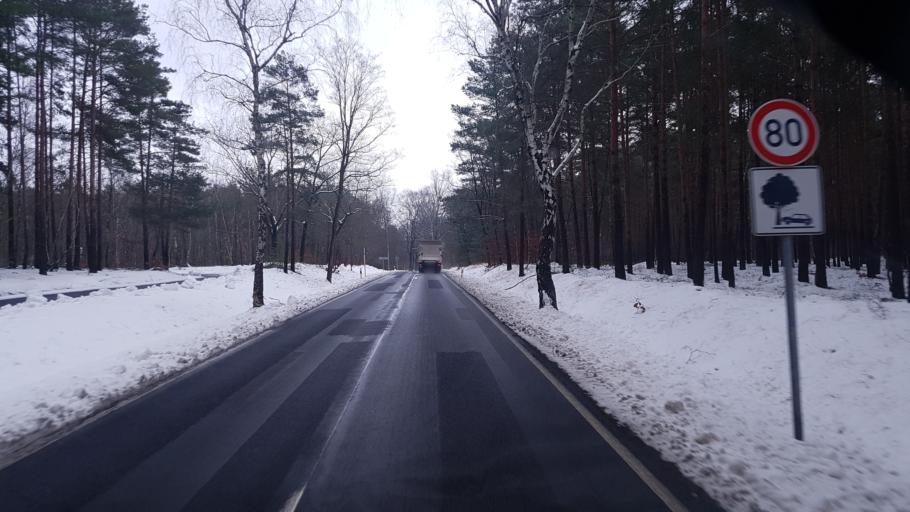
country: DE
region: Brandenburg
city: Lawitz
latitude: 52.0827
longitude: 14.5176
